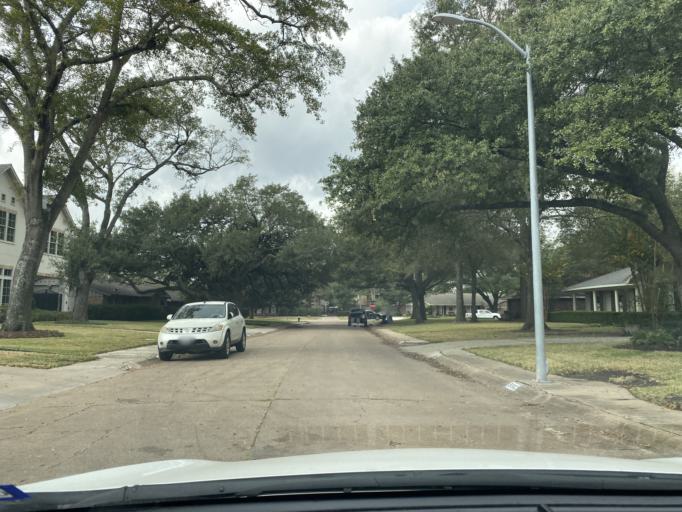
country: US
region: Texas
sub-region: Harris County
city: Hunters Creek Village
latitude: 29.7470
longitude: -95.4763
